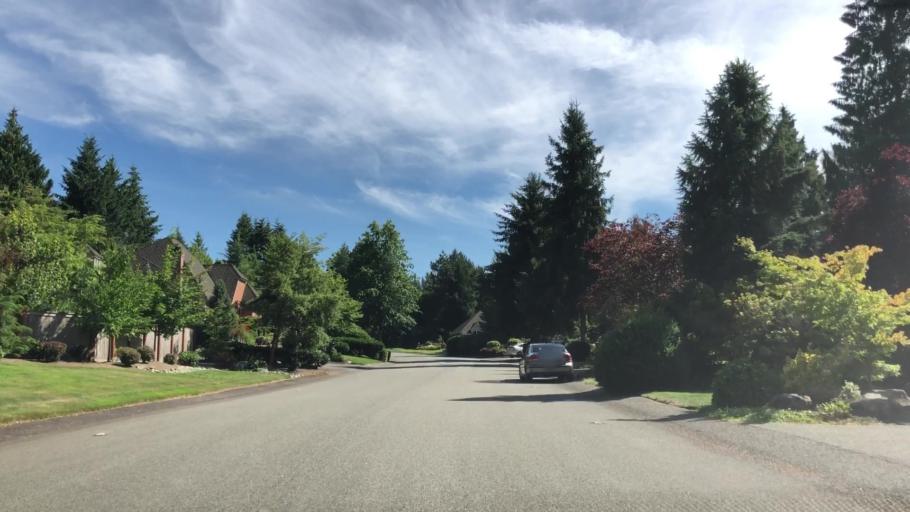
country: US
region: Washington
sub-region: King County
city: Cottage Lake
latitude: 47.7122
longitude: -122.0750
